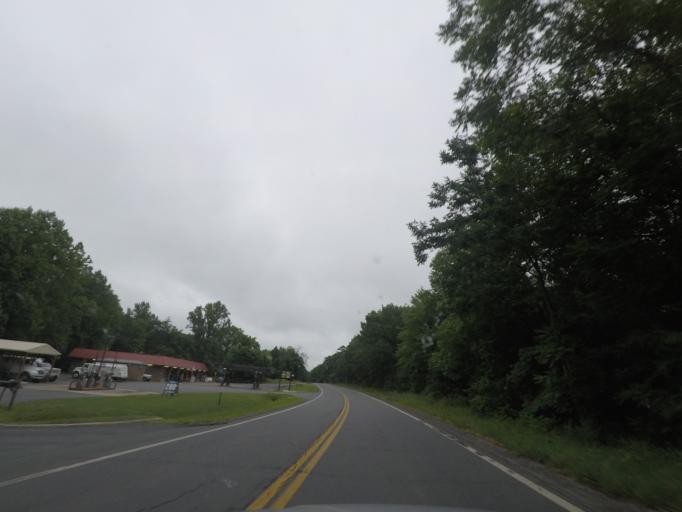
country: US
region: Virginia
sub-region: Fluvanna County
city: Weber City
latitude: 37.6842
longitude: -78.3292
